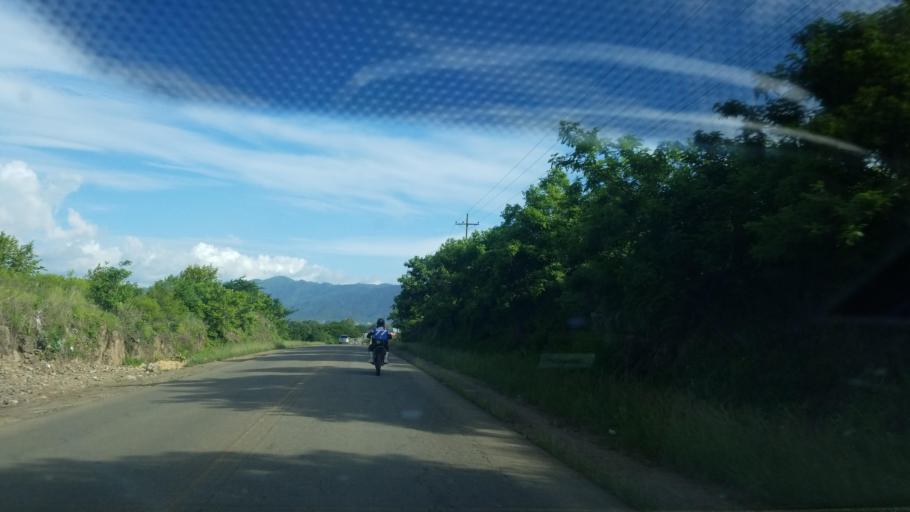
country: HN
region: El Paraiso
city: Cuyali
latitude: 13.9055
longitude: -86.5561
